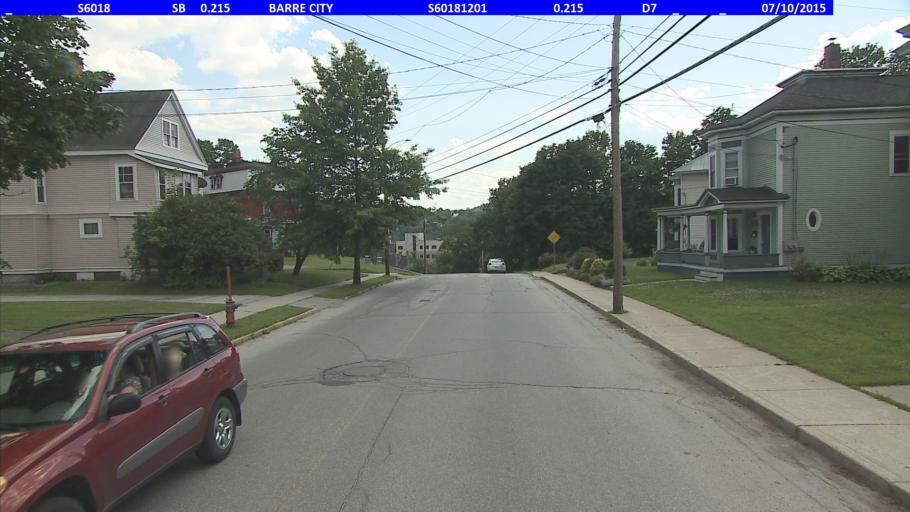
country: US
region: Vermont
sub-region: Washington County
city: Barre
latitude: 44.2021
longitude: -72.5021
